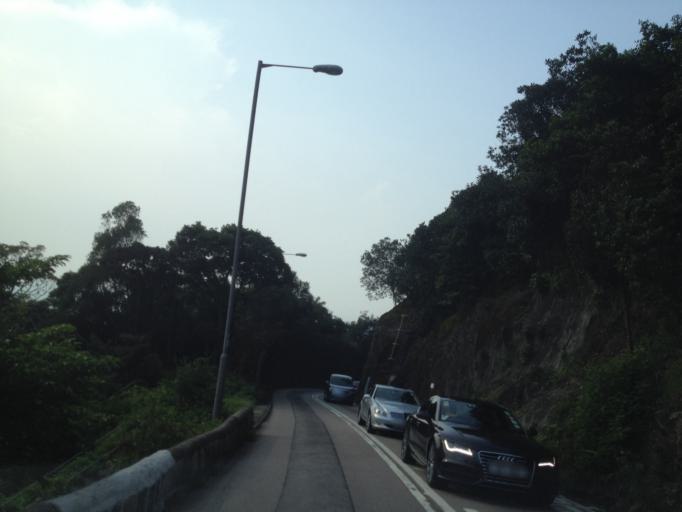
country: HK
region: Wanchai
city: Wan Chai
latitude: 22.2509
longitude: 114.2240
